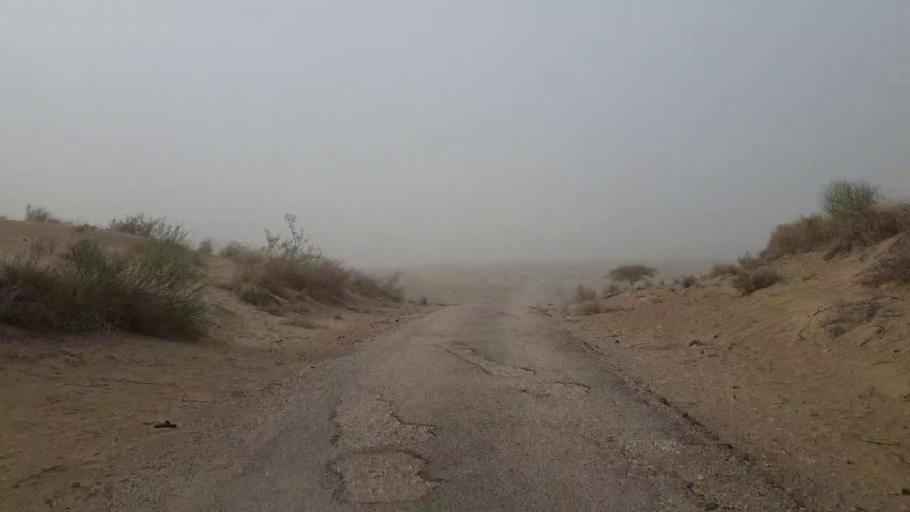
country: PK
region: Sindh
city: Islamkot
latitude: 24.5661
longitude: 70.3629
